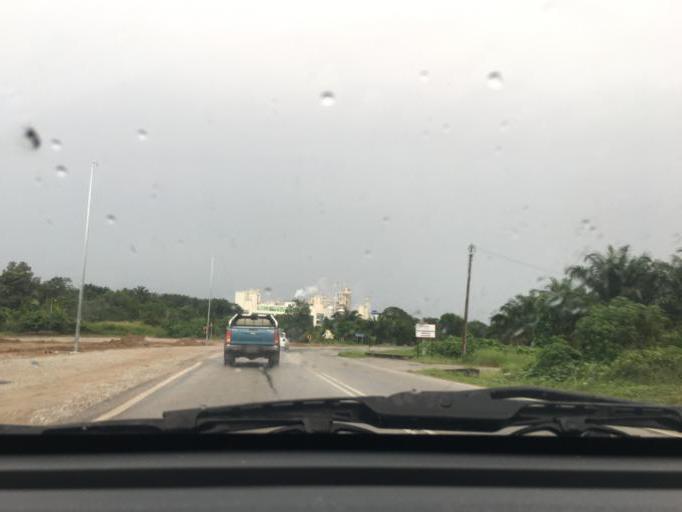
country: MY
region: Kedah
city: Sungai Petani
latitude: 5.6047
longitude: 100.6404
